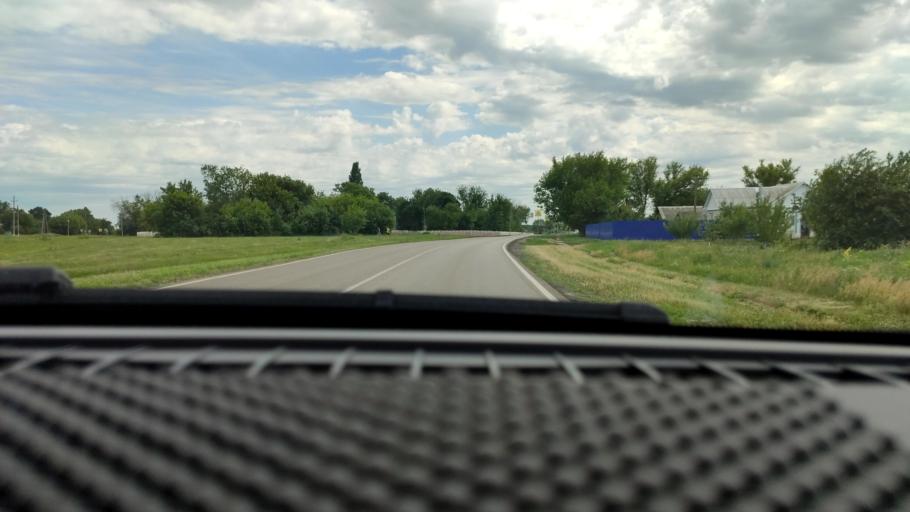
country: RU
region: Voronezj
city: Verkhnyaya Khava
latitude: 51.6799
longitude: 39.9415
